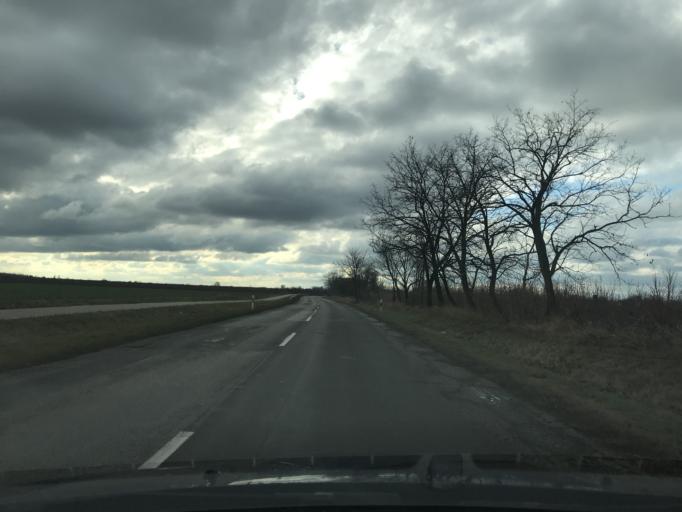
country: HU
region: Bacs-Kiskun
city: Hajos
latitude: 46.3809
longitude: 19.1426
